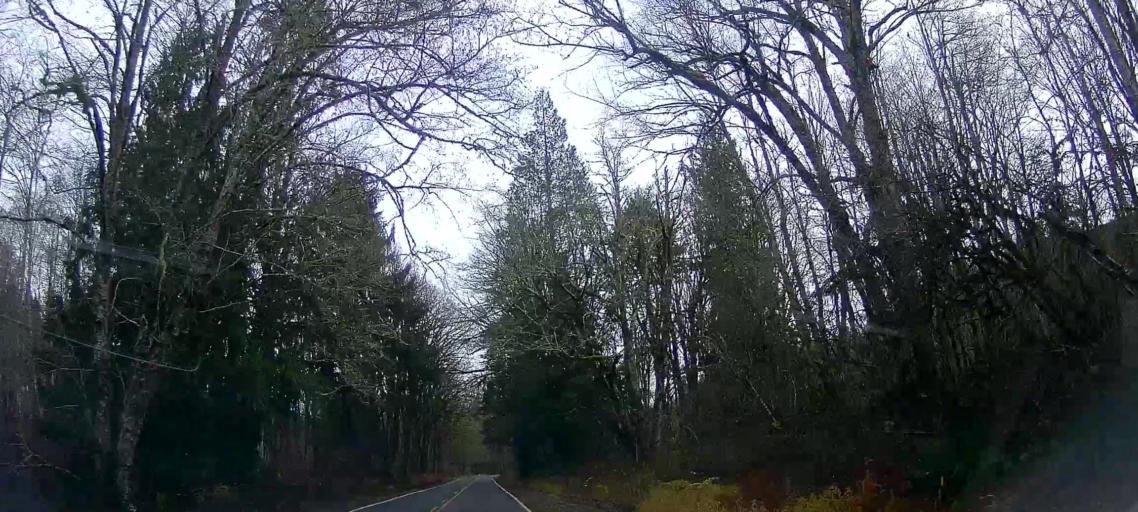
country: US
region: Washington
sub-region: Skagit County
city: Sedro-Woolley
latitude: 48.5163
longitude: -121.8684
